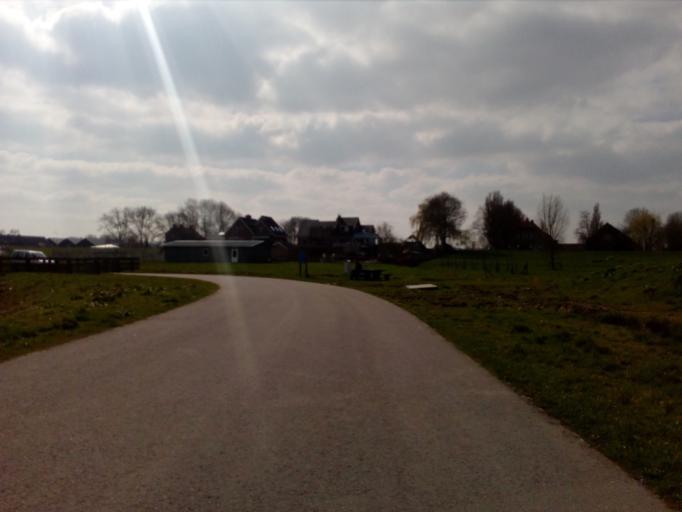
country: NL
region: South Holland
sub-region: Gemeente Zoetermeer
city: Zoetermeer
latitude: 52.0692
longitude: 4.4481
